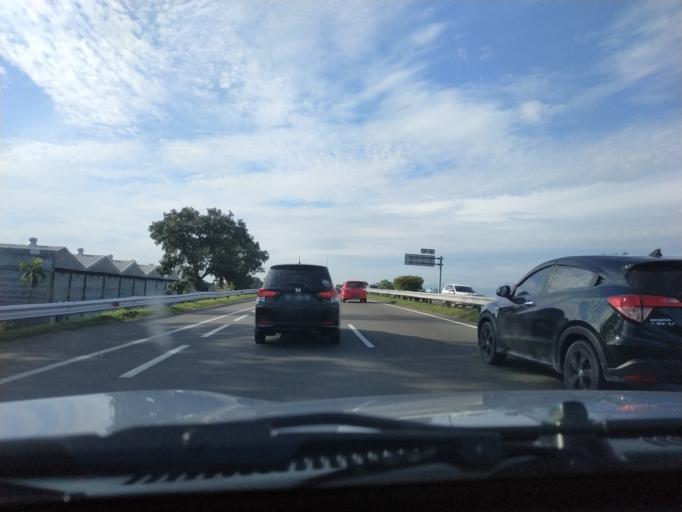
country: ID
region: North Sumatra
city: Medan
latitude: 3.5918
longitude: 98.7241
